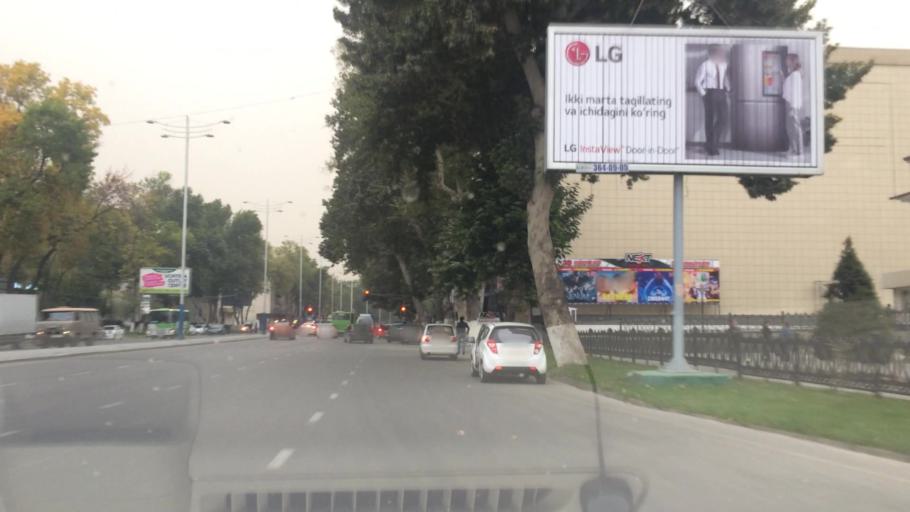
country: UZ
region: Toshkent Shahri
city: Tashkent
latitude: 41.2992
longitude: 69.2493
